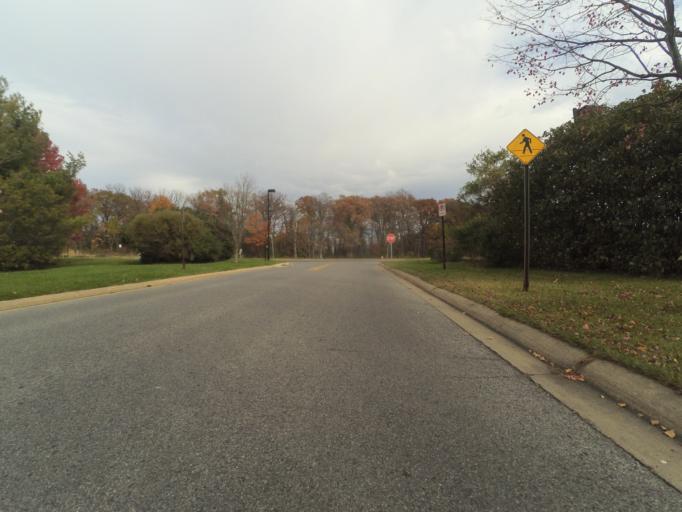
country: US
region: Pennsylvania
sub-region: Centre County
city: Lemont
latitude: 40.7843
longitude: -77.8194
